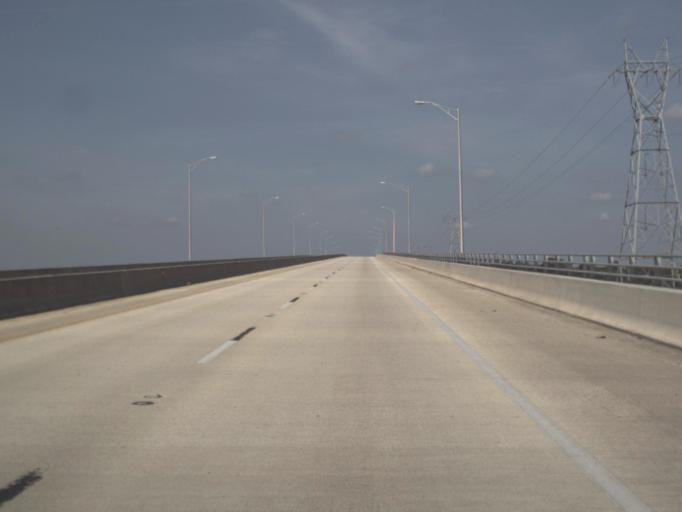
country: US
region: Florida
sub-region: Duval County
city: Atlantic Beach
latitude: 30.3630
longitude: -81.4376
